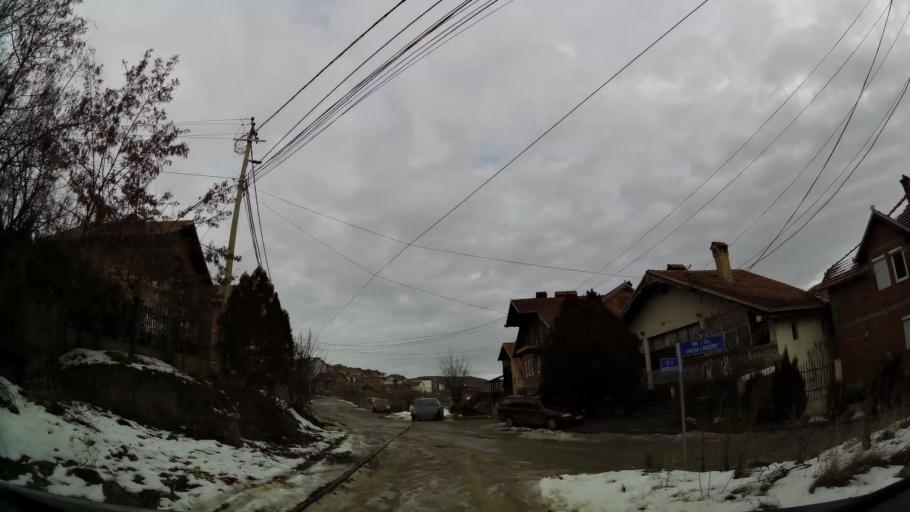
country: XK
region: Pristina
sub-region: Komuna e Prishtines
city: Pristina
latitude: 42.6833
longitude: 21.1739
